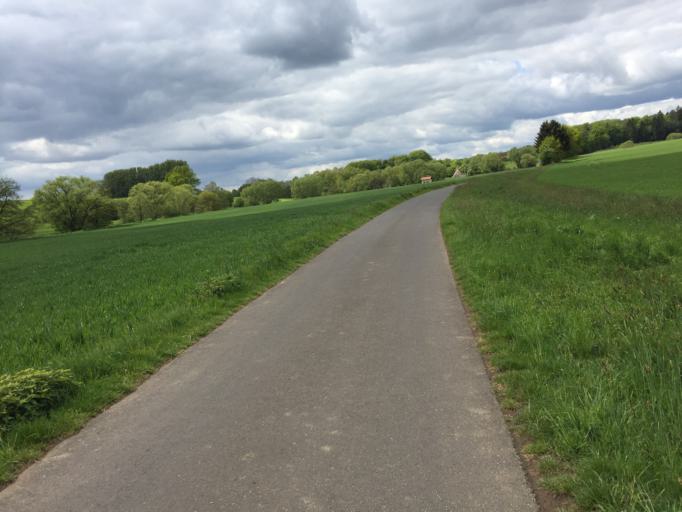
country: DE
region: Hesse
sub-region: Regierungsbezirk Giessen
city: Grunberg
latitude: 50.5715
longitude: 8.9146
